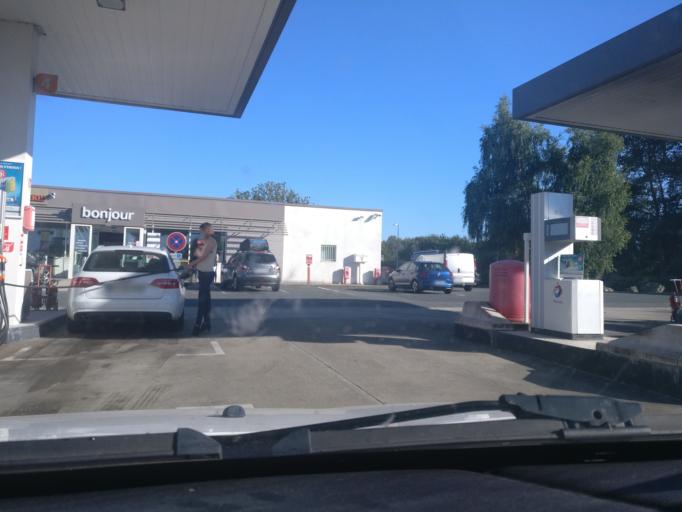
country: FR
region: Brittany
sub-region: Departement des Cotes-d'Armor
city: Saint-Agathon
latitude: 48.5504
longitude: -3.1128
